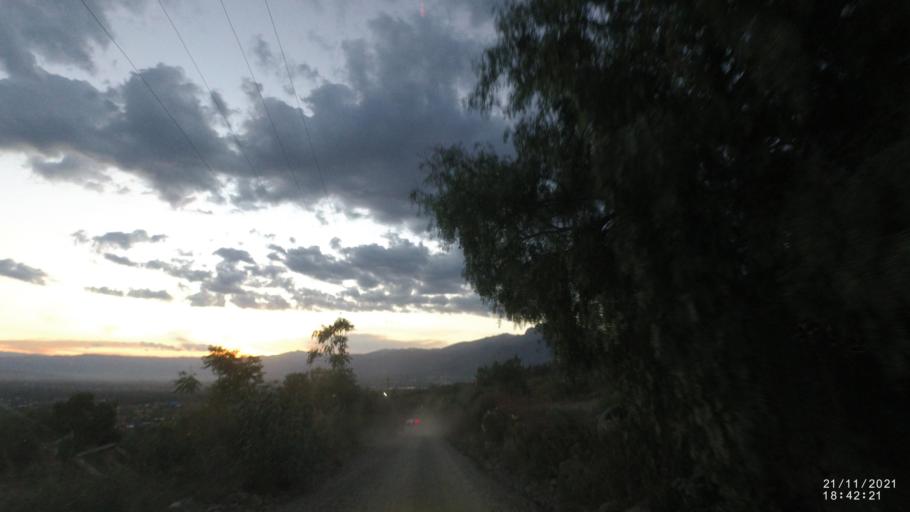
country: BO
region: Cochabamba
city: Cochabamba
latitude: -17.3198
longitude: -66.2177
